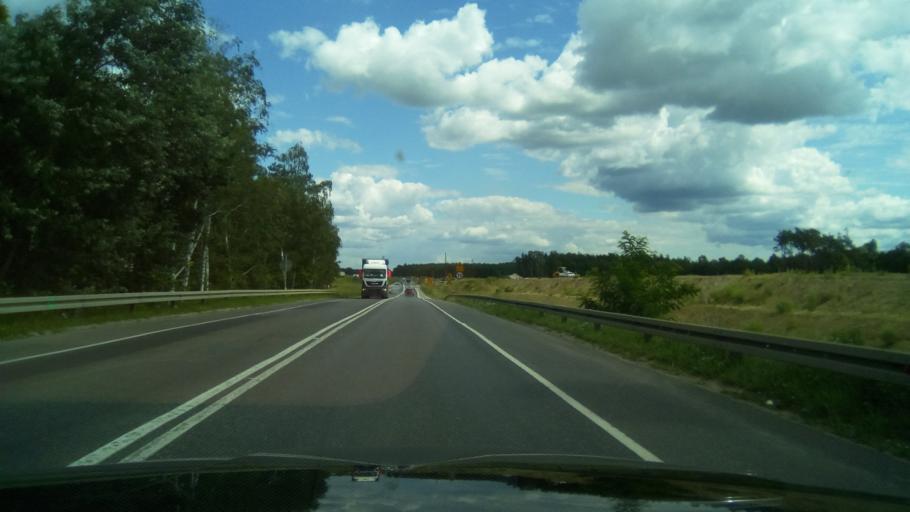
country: PL
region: Kujawsko-Pomorskie
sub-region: Powiat bydgoski
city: Biale Blota
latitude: 53.0763
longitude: 17.8441
